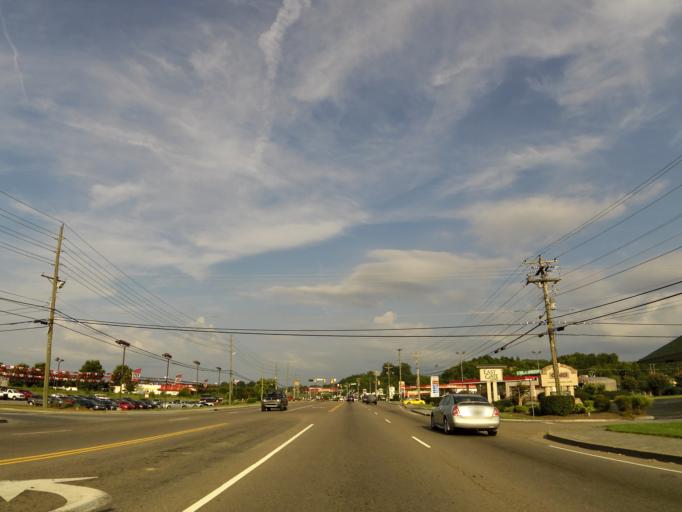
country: US
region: Tennessee
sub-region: Sevier County
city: Sevierville
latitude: 35.8649
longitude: -83.5482
